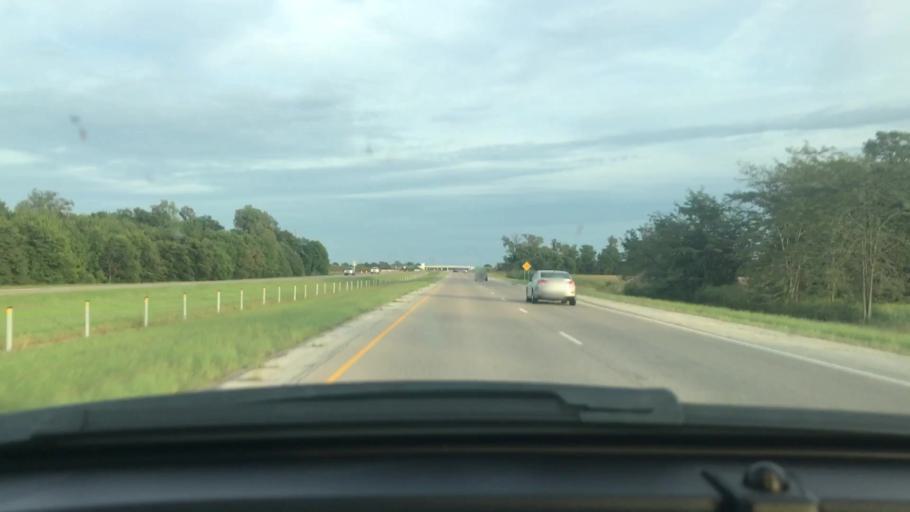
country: US
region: Arkansas
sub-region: Craighead County
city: Bay
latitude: 35.7814
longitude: -90.5960
